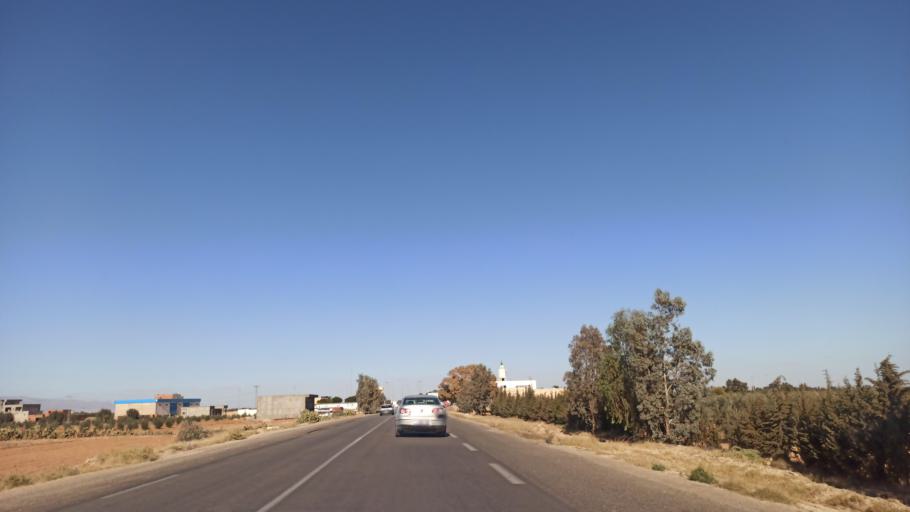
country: TN
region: Sidi Bu Zayd
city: Jilma
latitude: 35.1438
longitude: 9.3623
